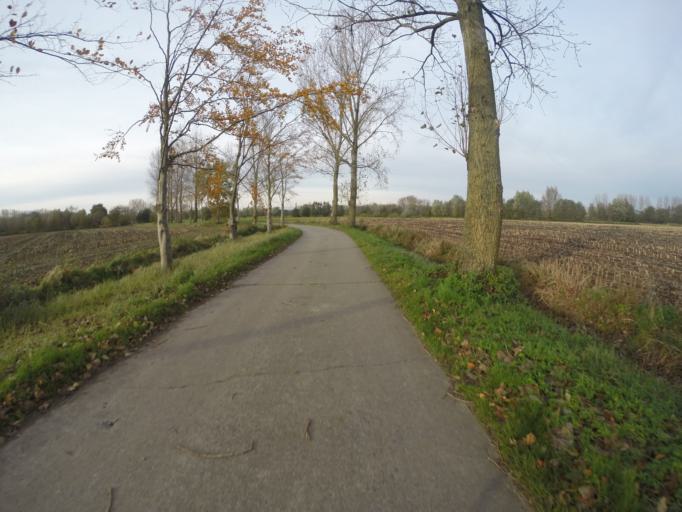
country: BE
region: Flanders
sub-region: Provincie Oost-Vlaanderen
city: Nevele
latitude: 51.0649
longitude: 3.5119
